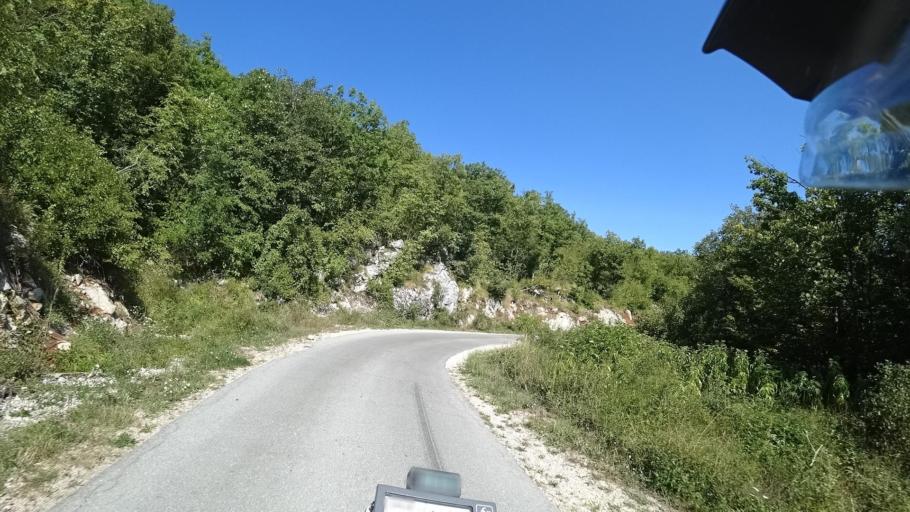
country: HR
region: Licko-Senjska
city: Otocac
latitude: 44.7358
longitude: 15.3590
